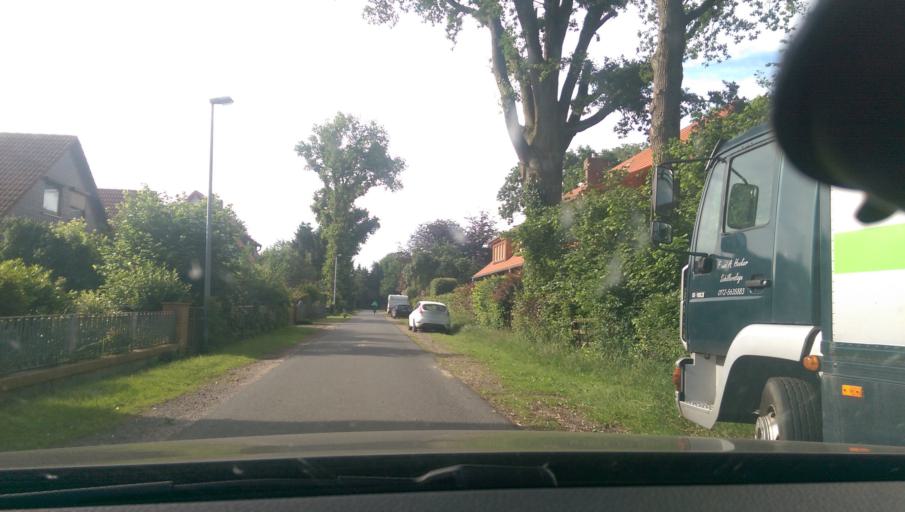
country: DE
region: Lower Saxony
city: Wietze
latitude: 52.5628
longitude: 9.8472
